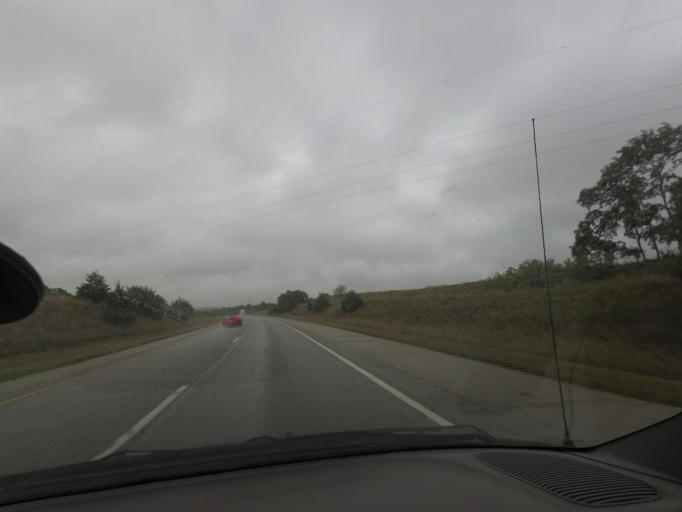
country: US
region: Illinois
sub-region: Pike County
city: Barry
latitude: 39.7282
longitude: -91.1220
